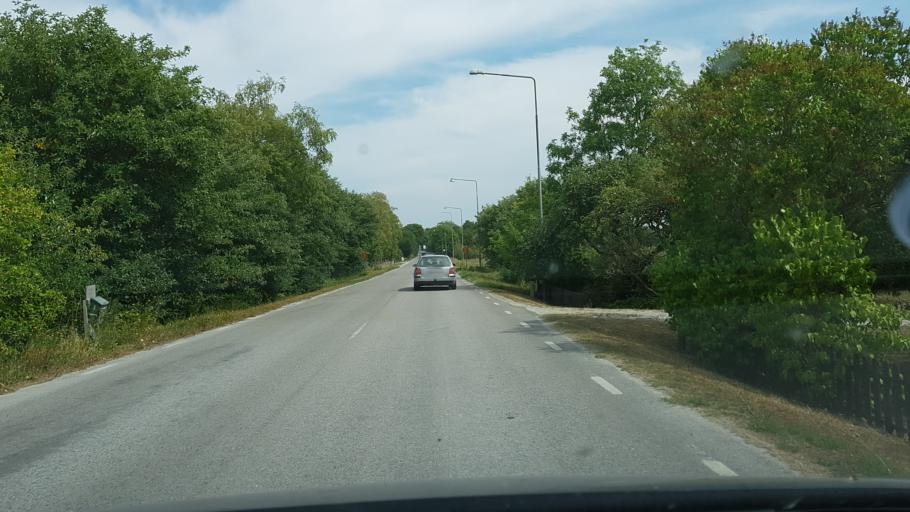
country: SE
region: Gotland
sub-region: Gotland
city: Slite
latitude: 57.7215
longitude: 18.7834
